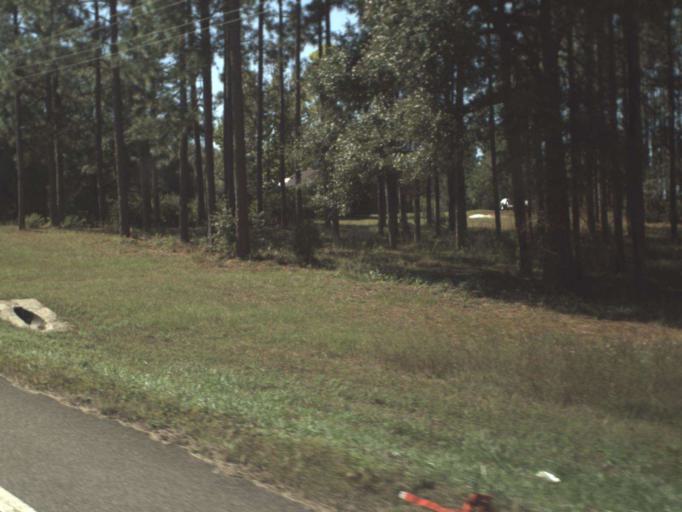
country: US
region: Alabama
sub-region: Geneva County
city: Samson
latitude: 30.9495
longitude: -86.1372
